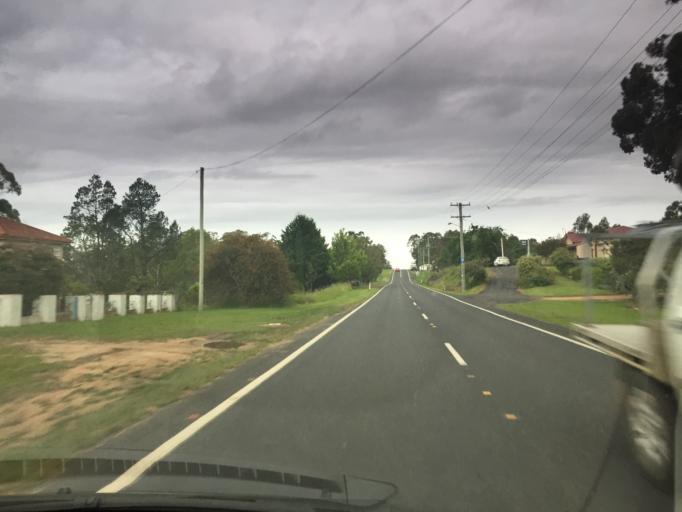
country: AU
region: New South Wales
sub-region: Bega Valley
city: Bega
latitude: -36.6293
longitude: 149.5723
